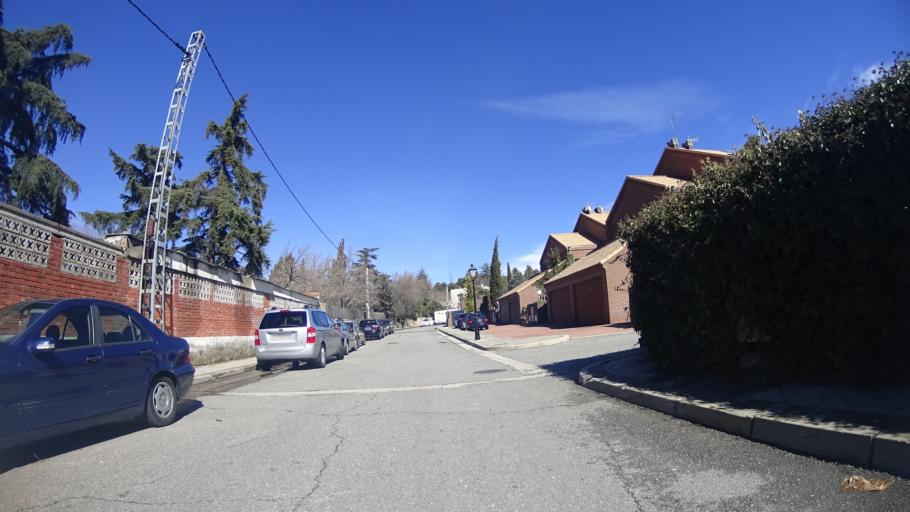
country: ES
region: Madrid
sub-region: Provincia de Madrid
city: Torrelodones
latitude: 40.5783
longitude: -3.9210
